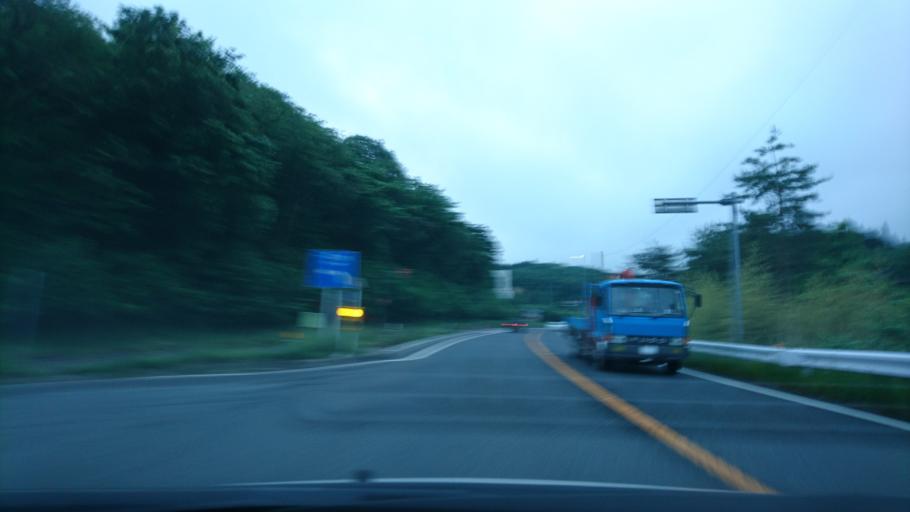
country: JP
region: Iwate
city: Ichinoseki
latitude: 38.8884
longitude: 141.1178
